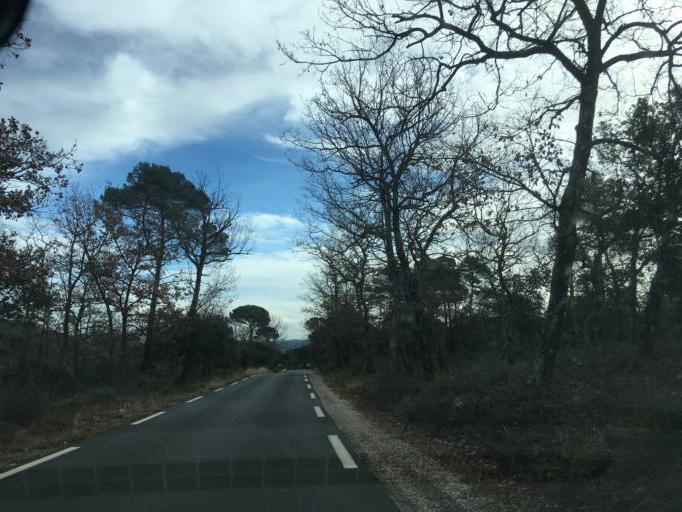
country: FR
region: Provence-Alpes-Cote d'Azur
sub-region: Departement du Var
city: Bras
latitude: 43.4478
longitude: 5.9909
